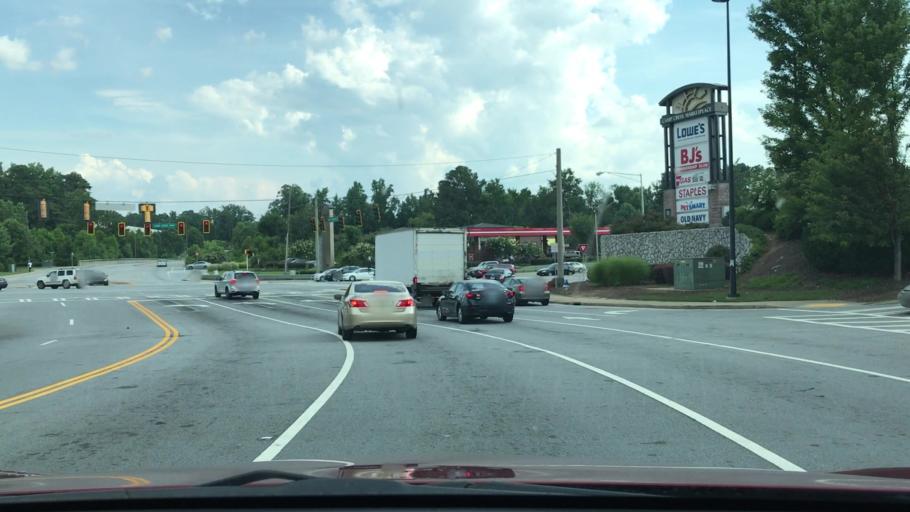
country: US
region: Georgia
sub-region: Fulton County
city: College Park
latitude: 33.6555
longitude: -84.5041
